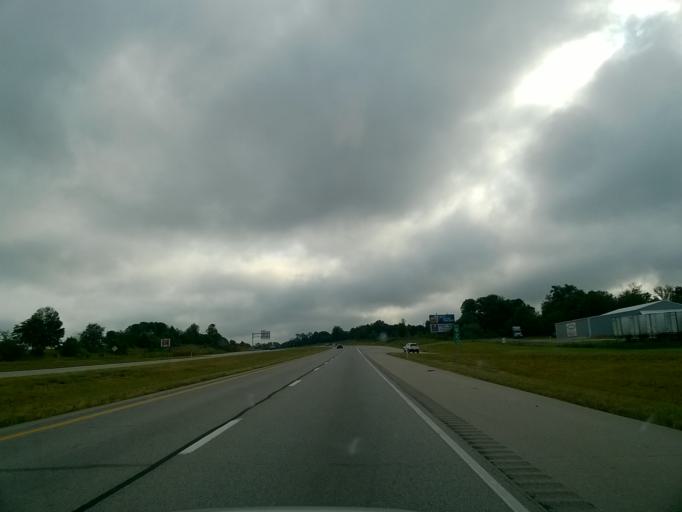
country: US
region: Indiana
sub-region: Crawford County
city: English
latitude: 38.2437
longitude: -86.3527
